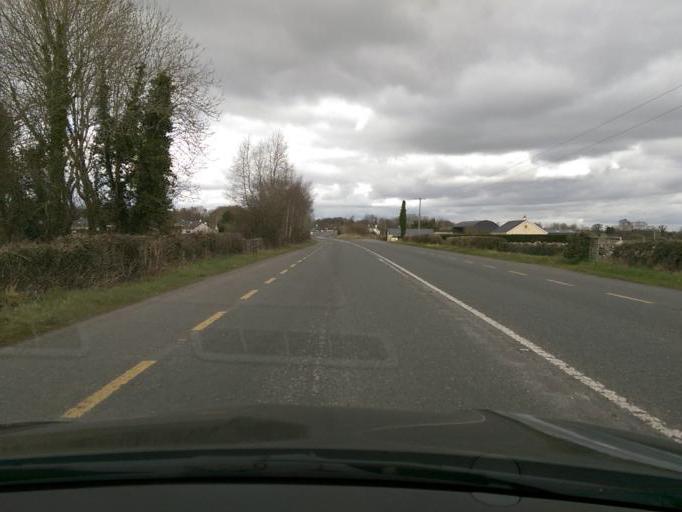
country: IE
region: Leinster
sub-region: An Iarmhi
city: Athlone
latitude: 53.3579
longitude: -8.0733
